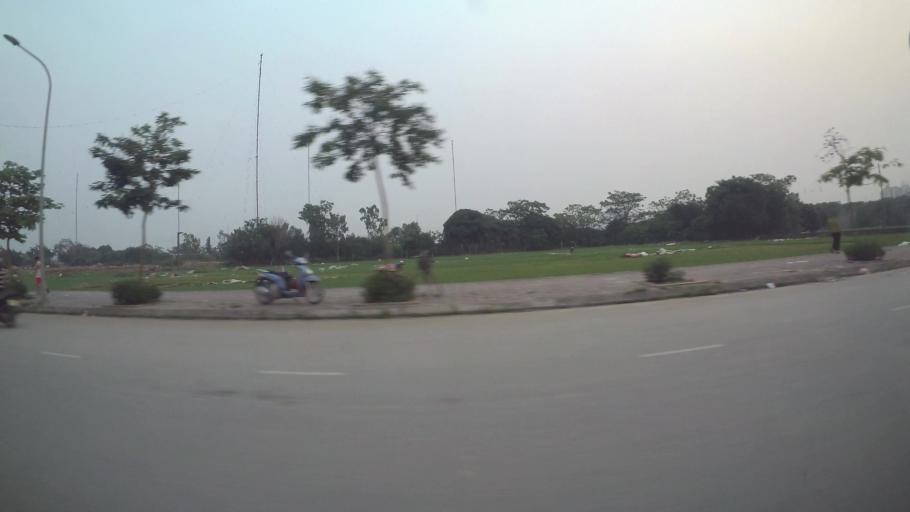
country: VN
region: Ha Noi
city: Thanh Xuan
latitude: 20.9775
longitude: 105.8007
